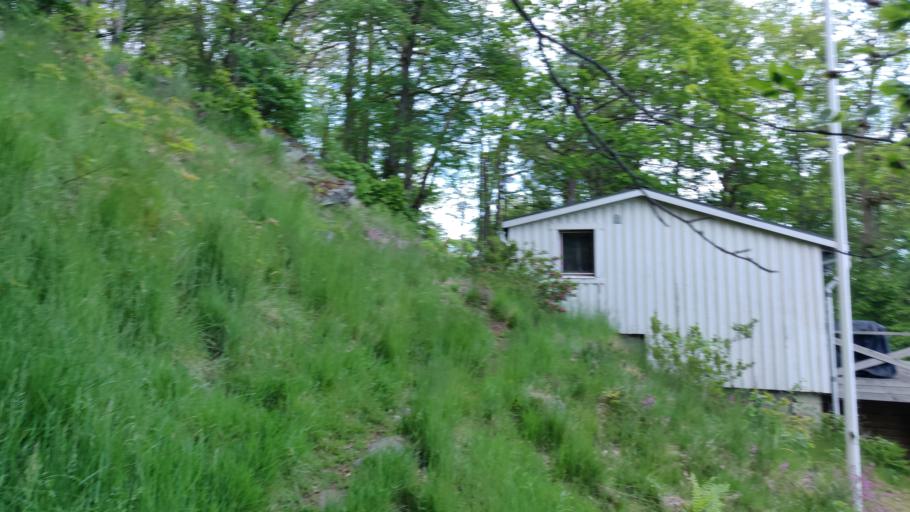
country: SE
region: Vaestra Goetaland
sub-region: Ulricehamns Kommun
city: Ulricehamn
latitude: 57.7837
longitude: 13.3856
